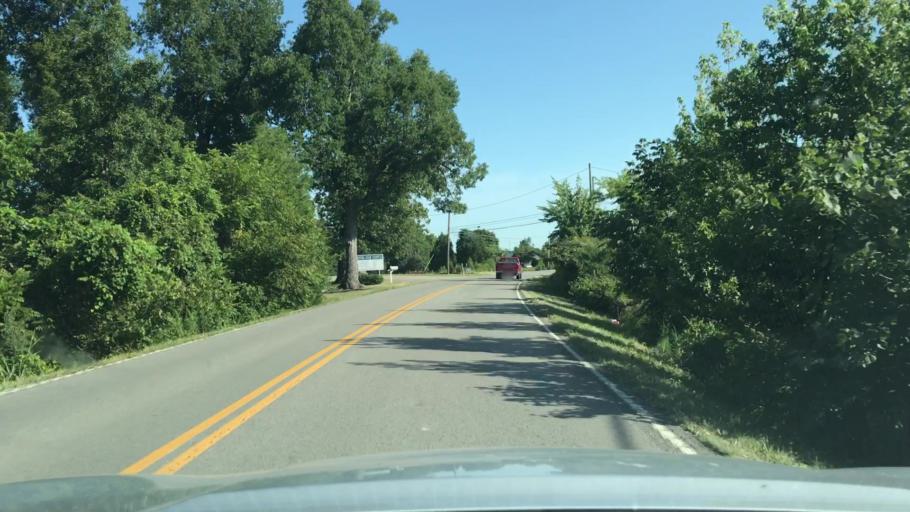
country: US
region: Kentucky
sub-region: Muhlenberg County
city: Greenville
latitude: 37.1735
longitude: -87.1526
